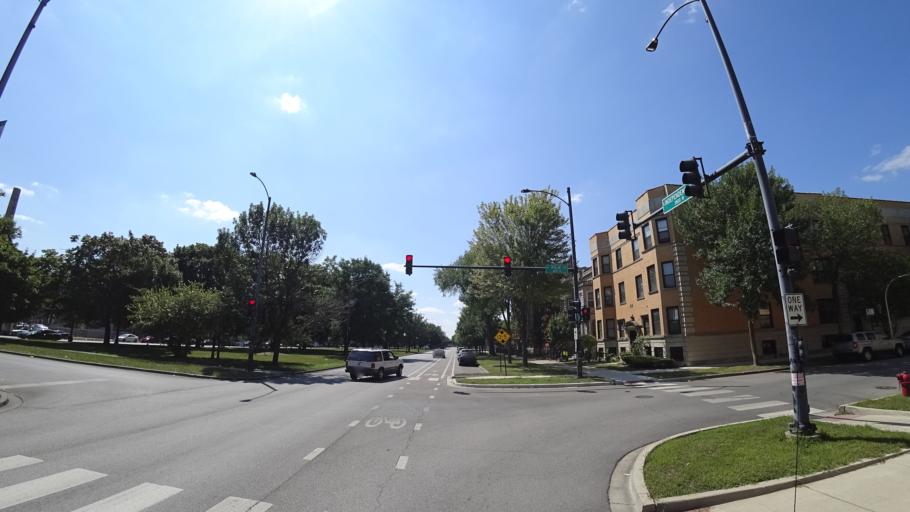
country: US
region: Illinois
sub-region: Cook County
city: Cicero
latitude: 41.8709
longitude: -87.7203
